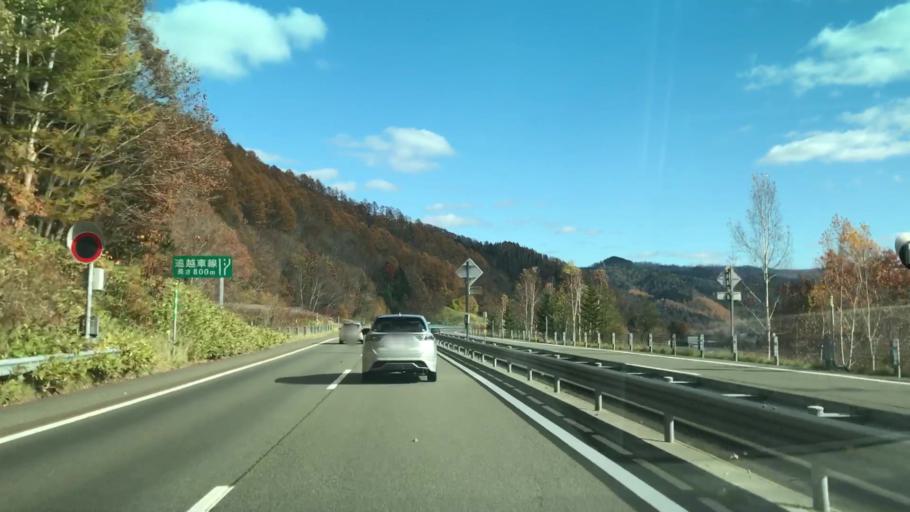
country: JP
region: Hokkaido
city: Chitose
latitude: 42.9081
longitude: 141.9910
